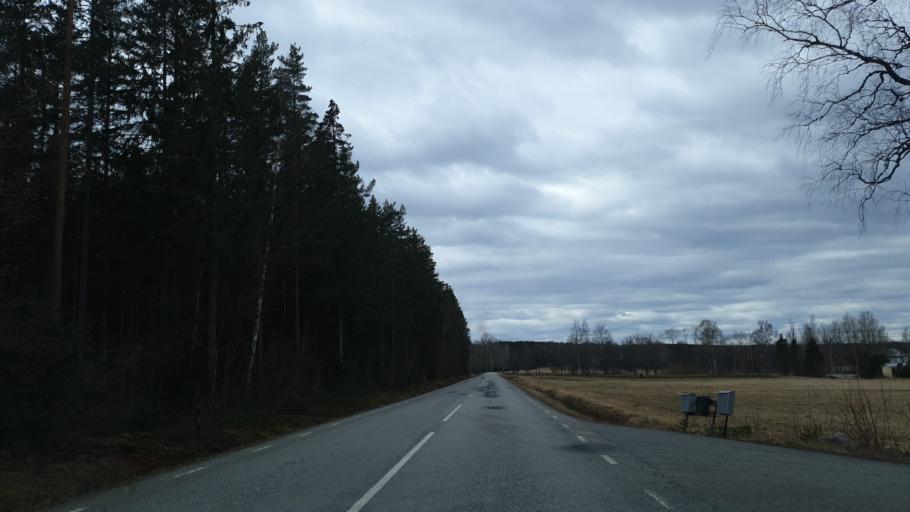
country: SE
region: OErebro
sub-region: Nora Kommun
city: As
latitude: 59.5811
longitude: 14.9756
